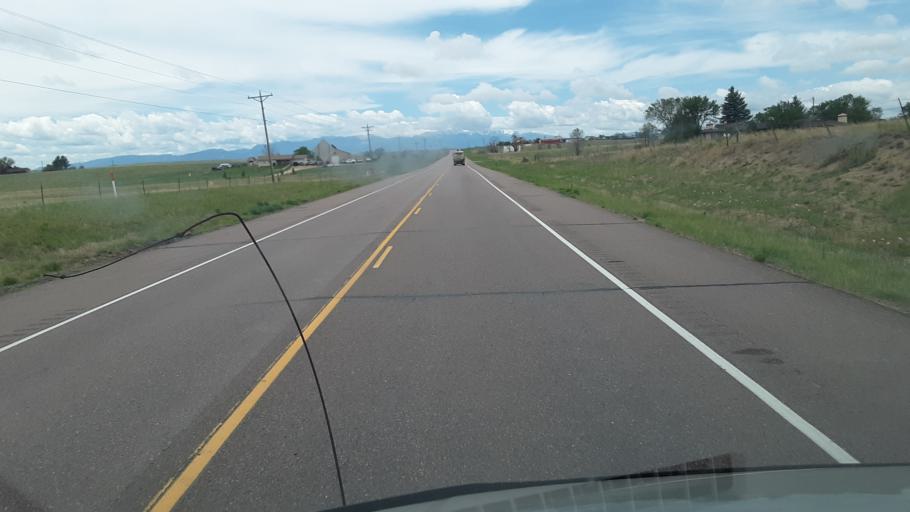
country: US
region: Colorado
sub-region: El Paso County
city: Ellicott
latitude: 38.8386
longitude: -104.4908
